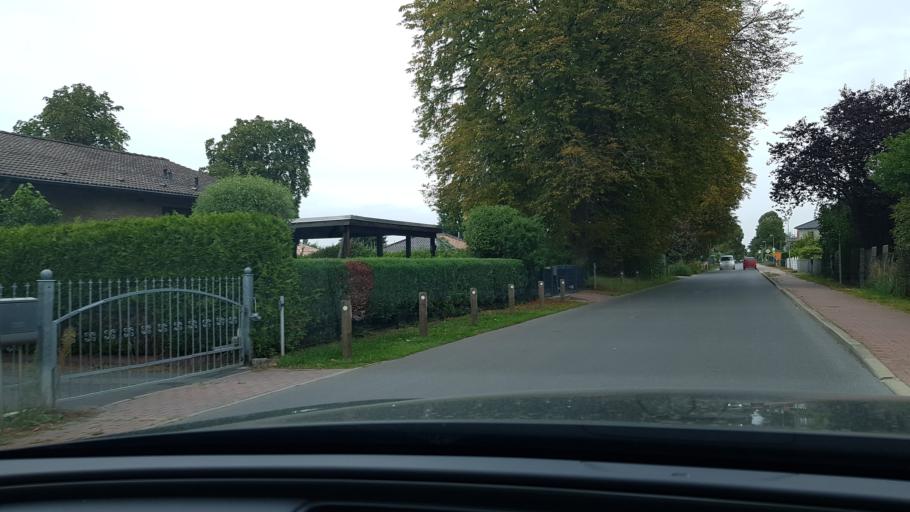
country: DE
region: Brandenburg
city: Brieselang
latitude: 52.5901
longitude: 12.9832
